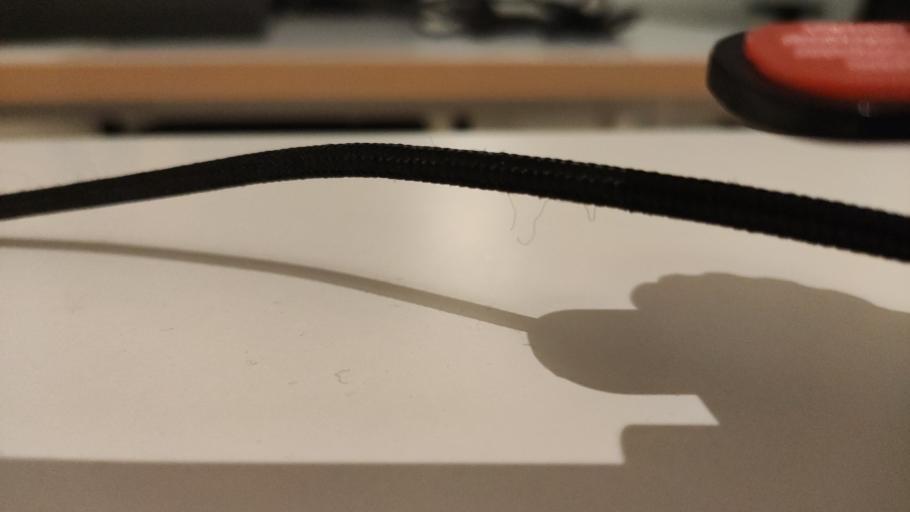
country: RU
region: Moskovskaya
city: Malino
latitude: 55.1082
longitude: 38.1162
